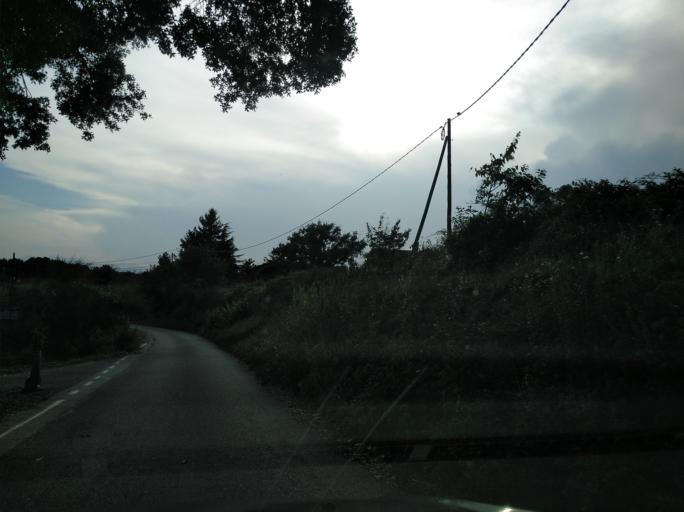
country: ES
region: Catalonia
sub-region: Provincia de Girona
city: Aiguaviva
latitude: 41.9392
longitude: 2.7674
